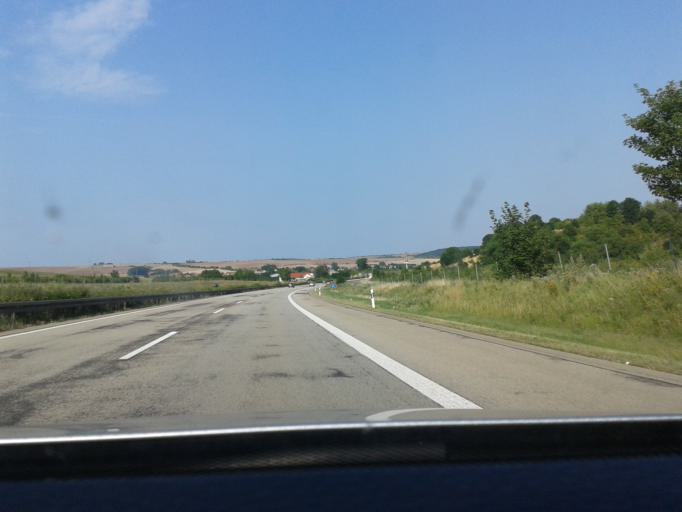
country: DE
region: Thuringia
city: Wipperdorf
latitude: 51.4406
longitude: 10.6490
